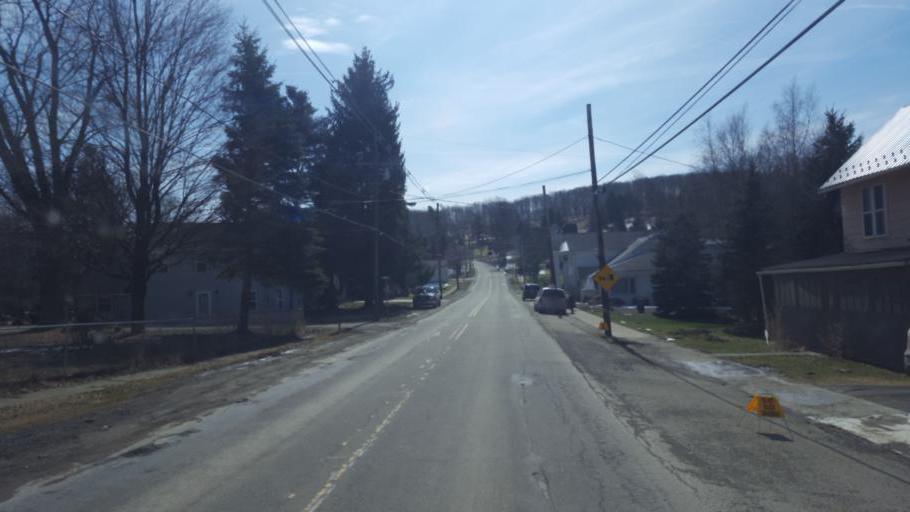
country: US
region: Pennsylvania
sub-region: Potter County
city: Galeton
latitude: 41.9006
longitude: -77.7622
